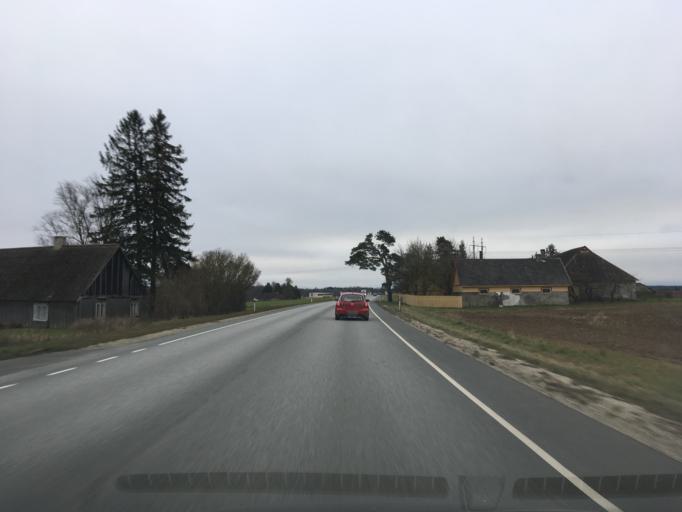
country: EE
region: Laeaene-Virumaa
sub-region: Someru vald
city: Someru
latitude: 59.3766
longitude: 26.4206
